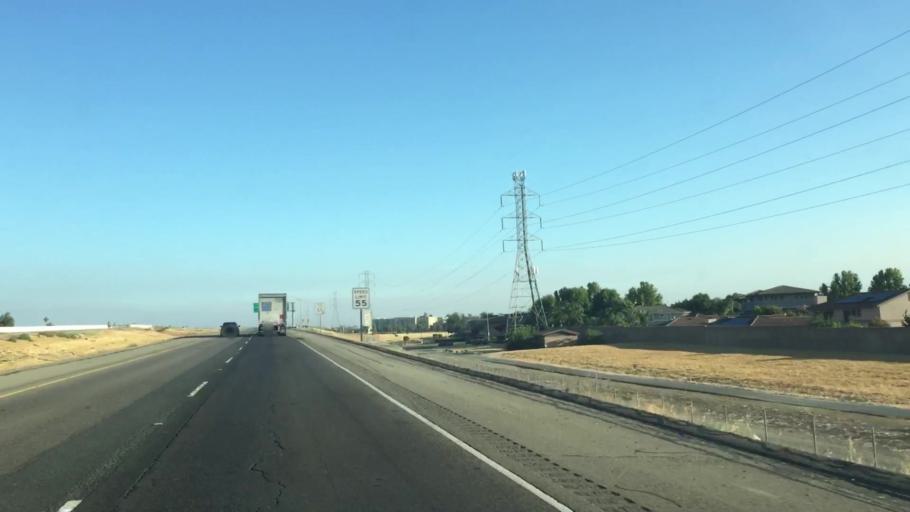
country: US
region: California
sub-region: Contra Costa County
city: Brentwood
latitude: 37.9377
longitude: -121.7386
